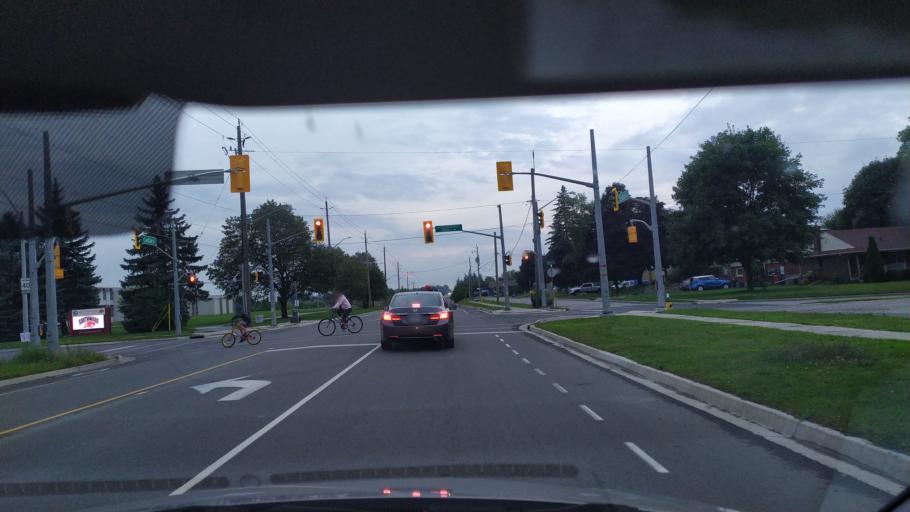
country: CA
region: Ontario
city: Cambridge
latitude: 43.3504
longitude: -80.3359
